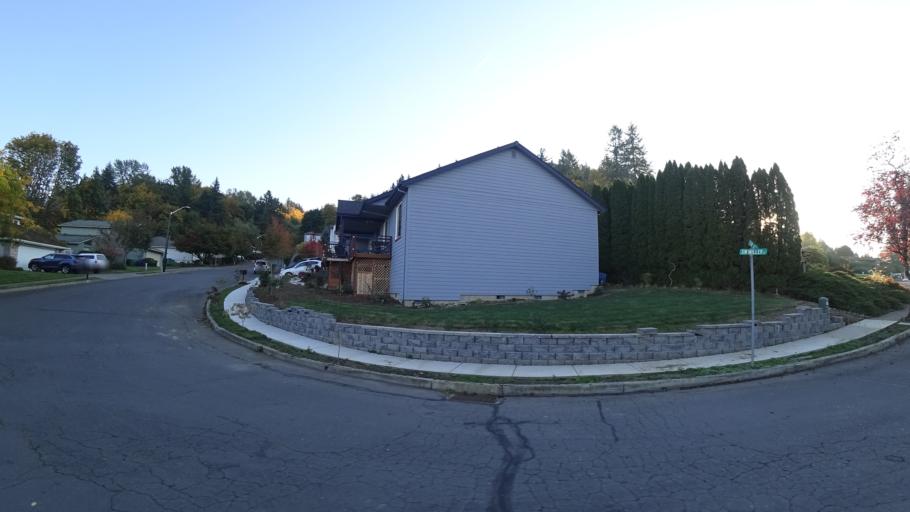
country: US
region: Oregon
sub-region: Multnomah County
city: Gresham
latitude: 45.4928
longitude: -122.4327
